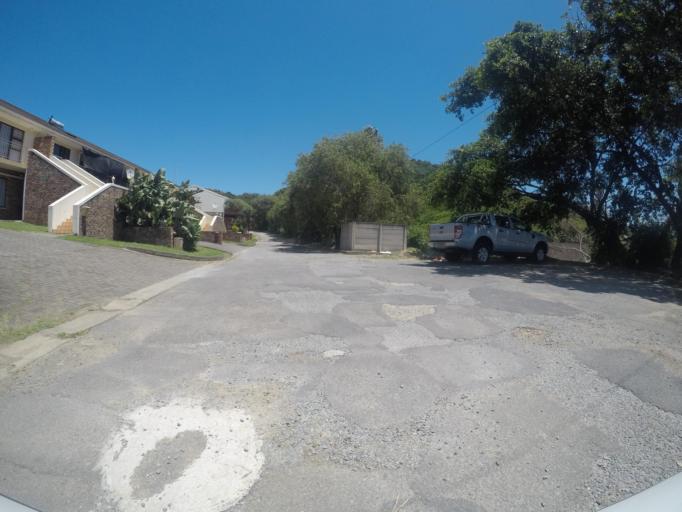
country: ZA
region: Eastern Cape
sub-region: Buffalo City Metropolitan Municipality
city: East London
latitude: -32.9347
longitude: 28.0103
